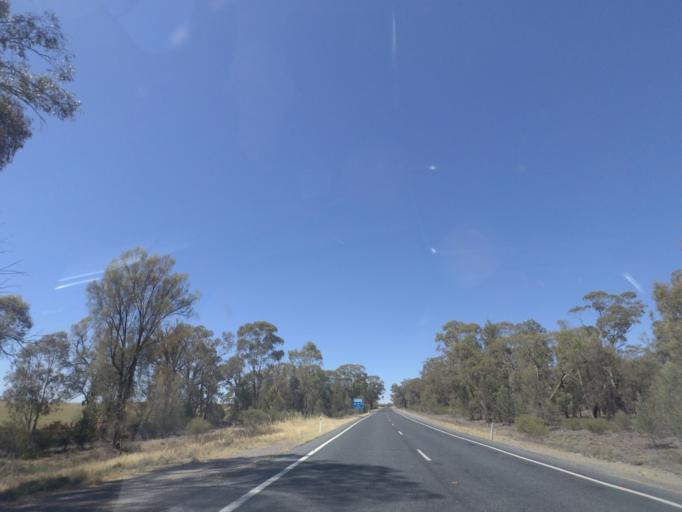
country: AU
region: New South Wales
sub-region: Narrandera
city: Narrandera
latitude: -34.4415
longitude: 146.8411
